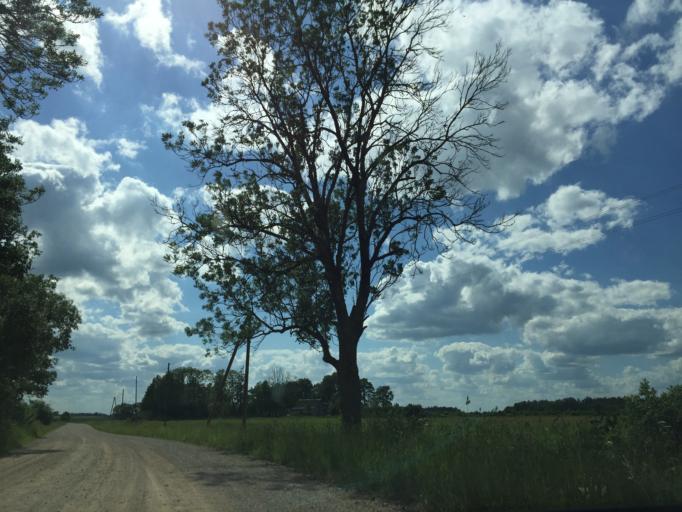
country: LV
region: Tukuma Rajons
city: Tukums
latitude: 56.9007
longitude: 23.1203
